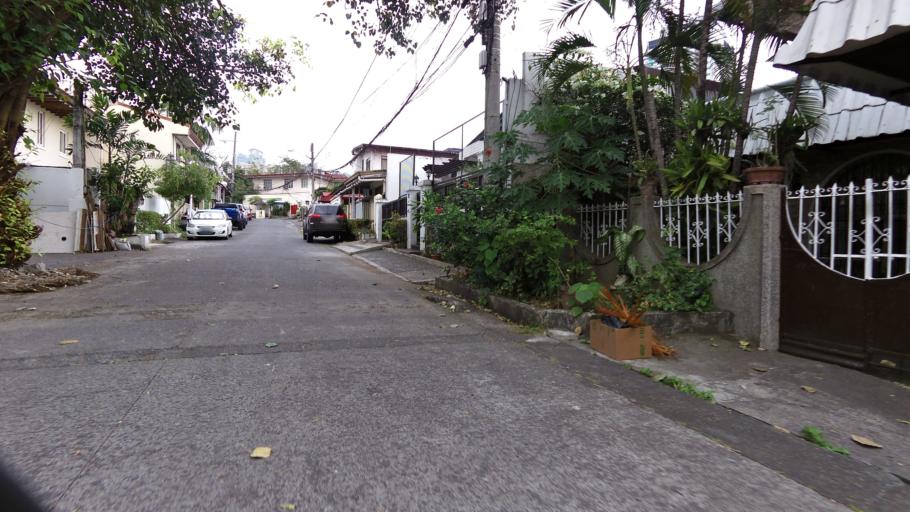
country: PH
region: Metro Manila
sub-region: Pasig
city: Pasig City
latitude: 14.5696
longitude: 121.0623
